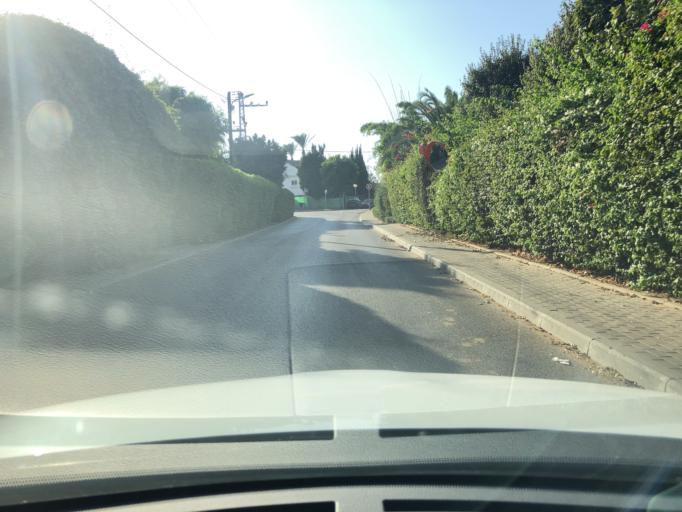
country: IL
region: Central District
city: Hod HaSharon
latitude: 32.1409
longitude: 34.9041
